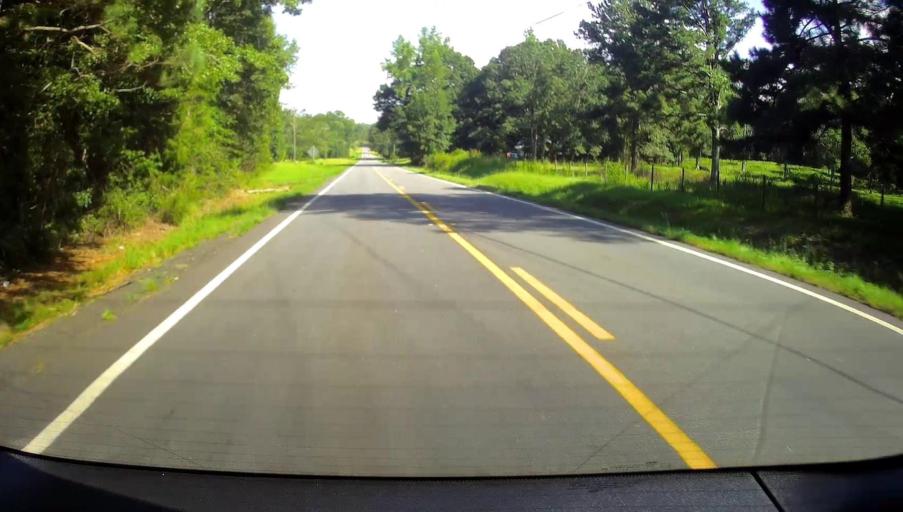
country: US
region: Georgia
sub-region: Upson County
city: Hannahs Mill
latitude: 32.9205
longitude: -84.4373
